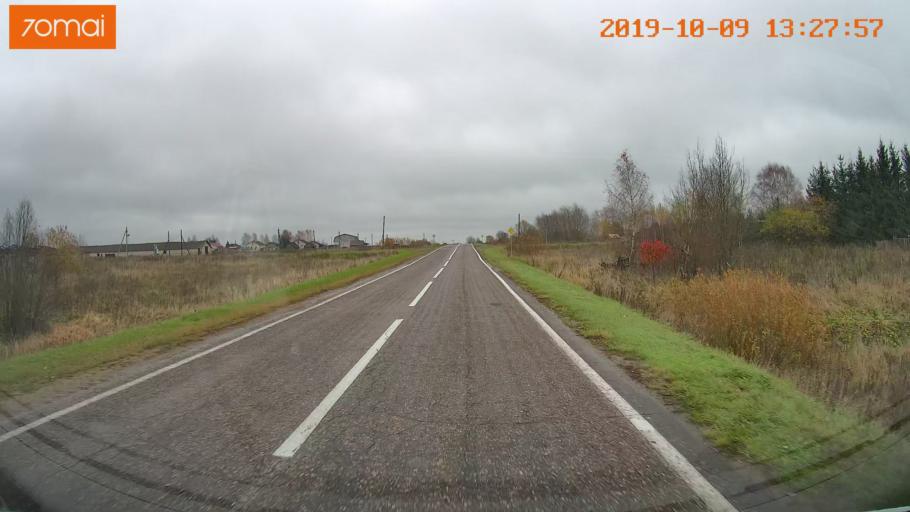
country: RU
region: Jaroslavl
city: Lyubim
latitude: 58.3149
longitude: 40.9576
